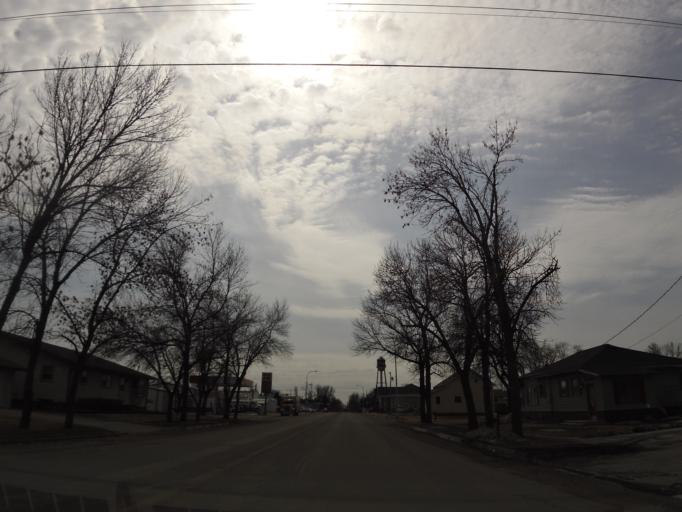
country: US
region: North Dakota
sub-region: Walsh County
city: Grafton
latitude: 48.2933
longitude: -97.3715
